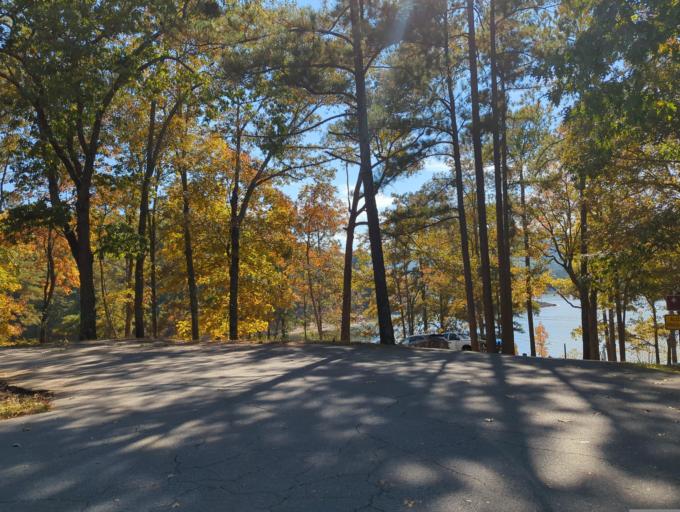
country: US
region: Georgia
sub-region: Bartow County
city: Emerson
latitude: 34.1504
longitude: -84.7167
